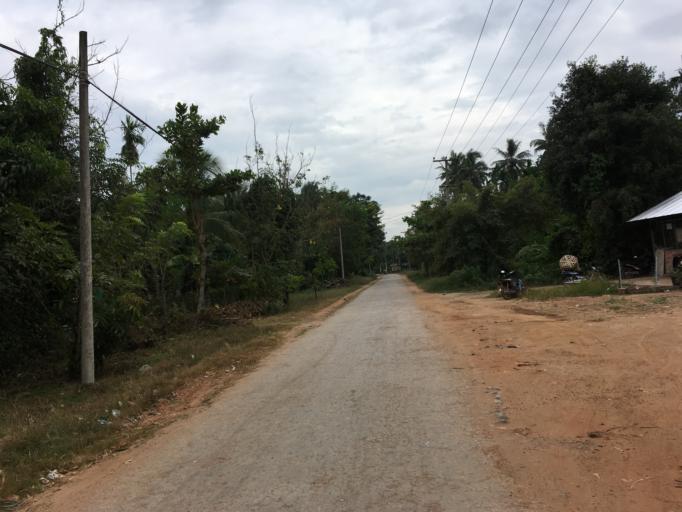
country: MM
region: Mon
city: Mawlamyine
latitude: 16.4270
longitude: 97.6323
